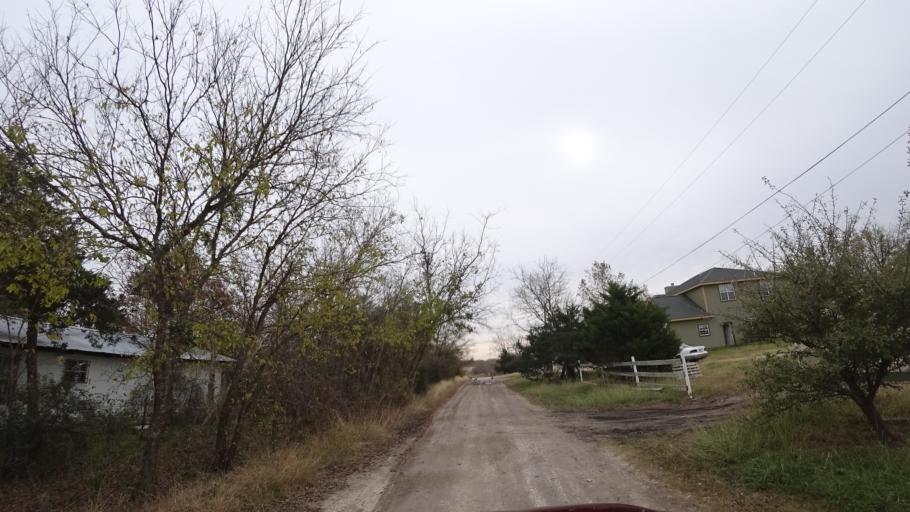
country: US
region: Texas
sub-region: Travis County
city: Garfield
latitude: 30.1087
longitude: -97.5880
